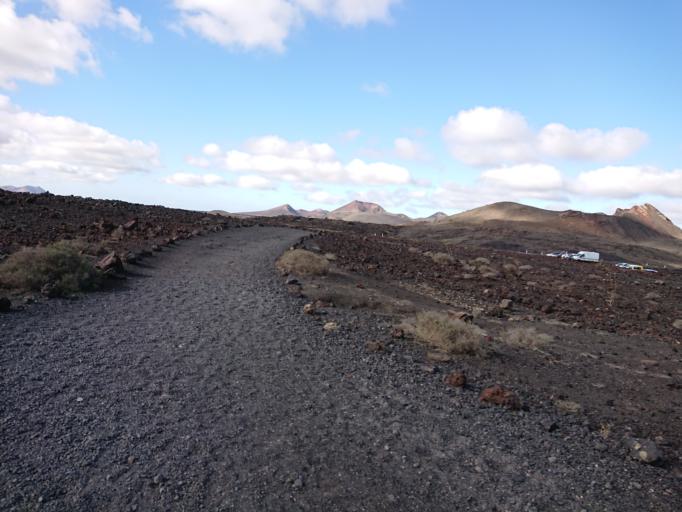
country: ES
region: Canary Islands
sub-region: Provincia de Las Palmas
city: Tias
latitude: 29.0042
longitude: -13.6826
